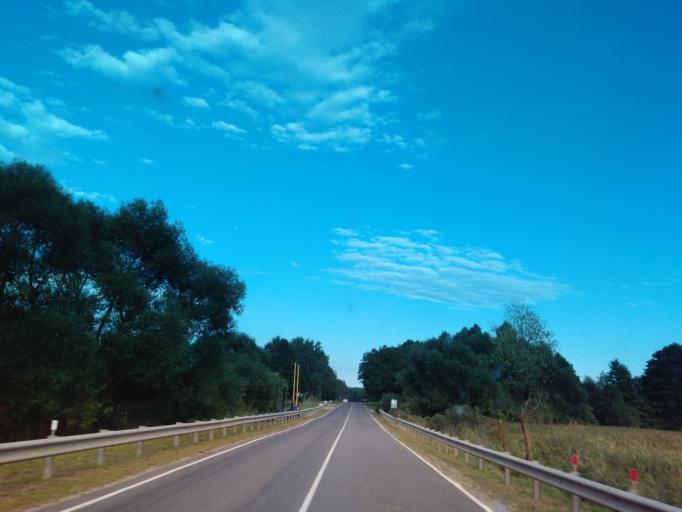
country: BY
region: Minsk
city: Uzda
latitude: 53.4203
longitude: 27.4041
